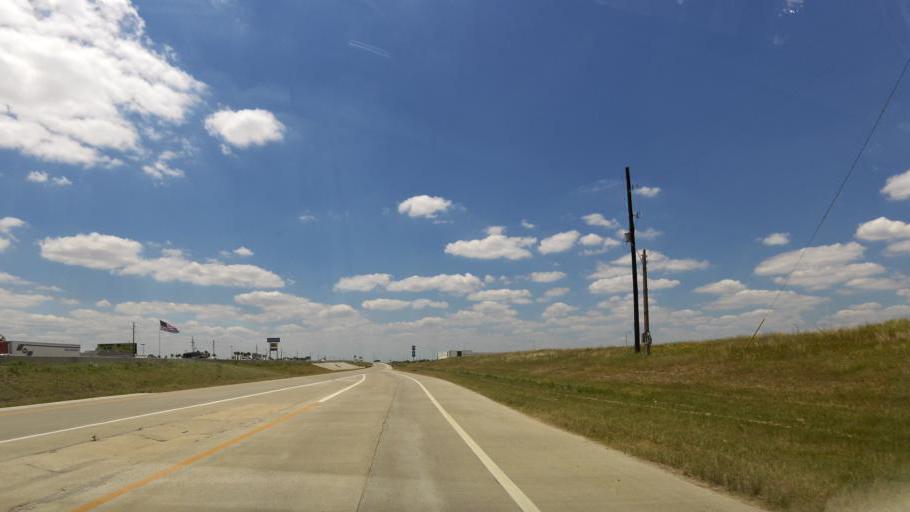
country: US
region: Texas
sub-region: Harris County
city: Katy
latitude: 29.7777
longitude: -95.8520
